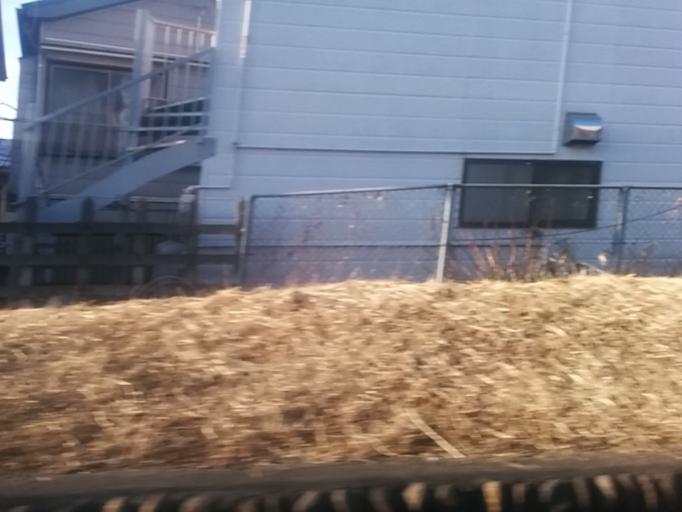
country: JP
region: Saitama
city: Wako
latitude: 35.7755
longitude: 139.6361
